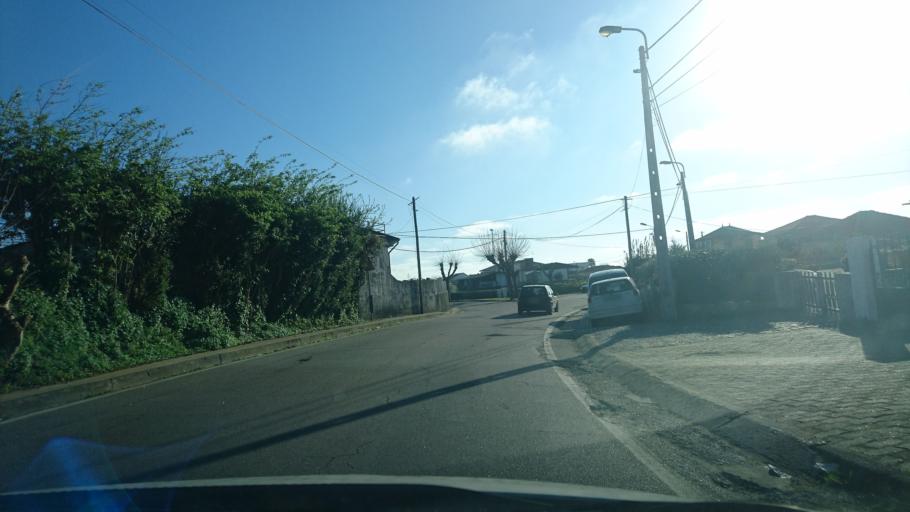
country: PT
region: Aveiro
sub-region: Espinho
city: Silvalde
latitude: 40.9876
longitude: -8.6307
